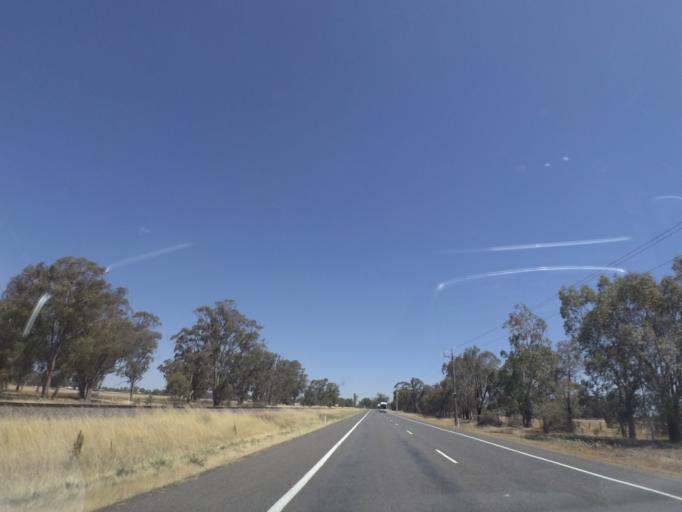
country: AU
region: Victoria
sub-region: Greater Shepparton
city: Shepparton
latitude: -36.2306
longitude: 145.4318
